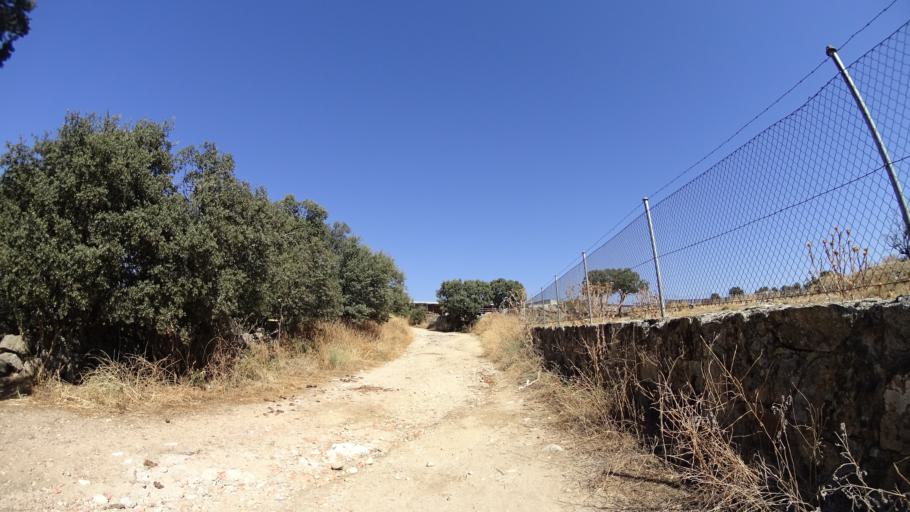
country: ES
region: Madrid
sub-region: Provincia de Madrid
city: Collado-Villalba
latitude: 40.6116
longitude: -4.0033
